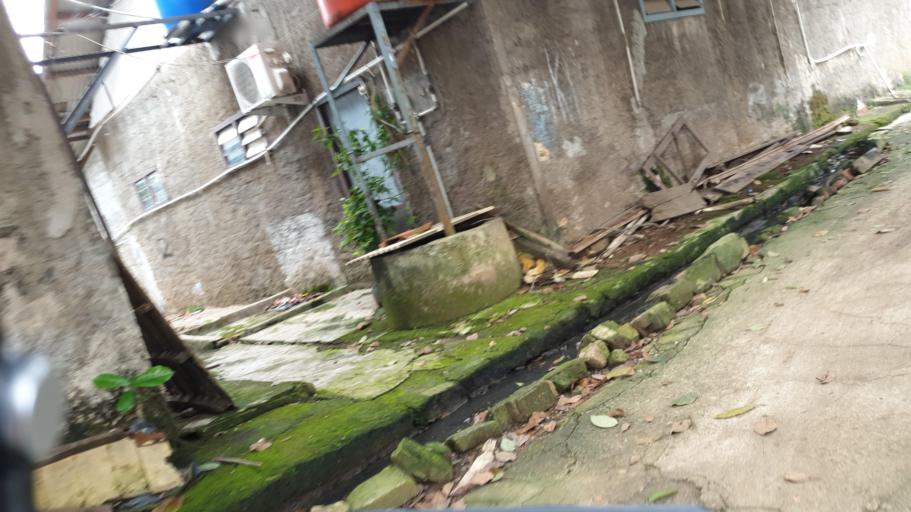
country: ID
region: West Java
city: Depok
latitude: -6.3233
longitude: 106.8260
